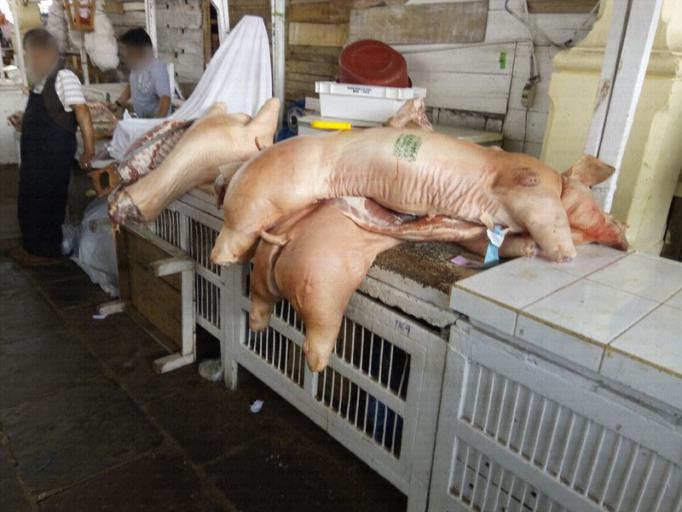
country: PE
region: Cusco
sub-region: Provincia de Cusco
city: Cusco
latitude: -13.5210
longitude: -71.9829
